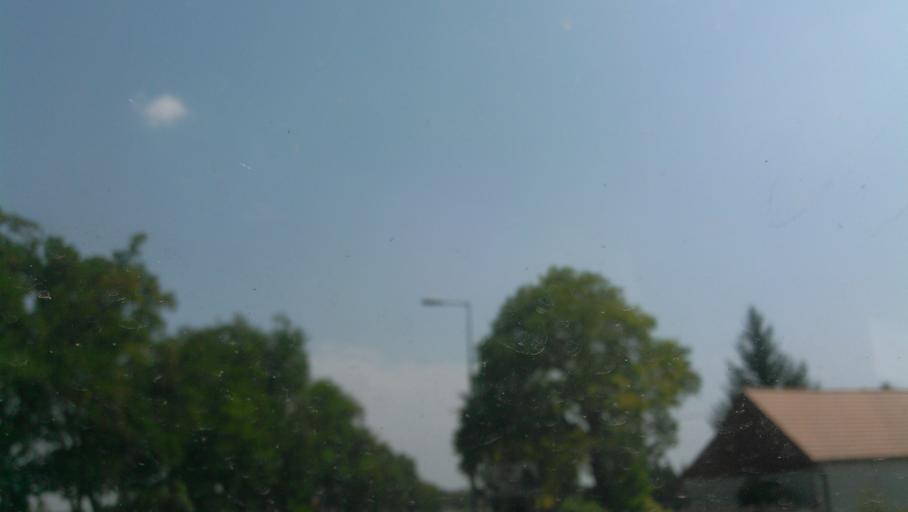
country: SK
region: Trnavsky
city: Samorin
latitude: 48.0552
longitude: 17.4461
